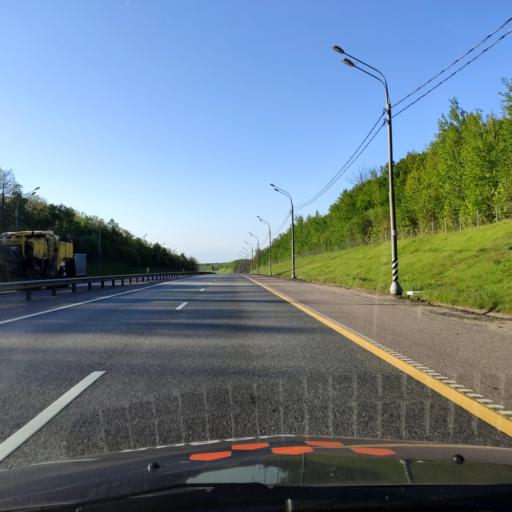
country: RU
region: Lipetsk
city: Zadonsk
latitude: 52.3989
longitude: 38.8598
